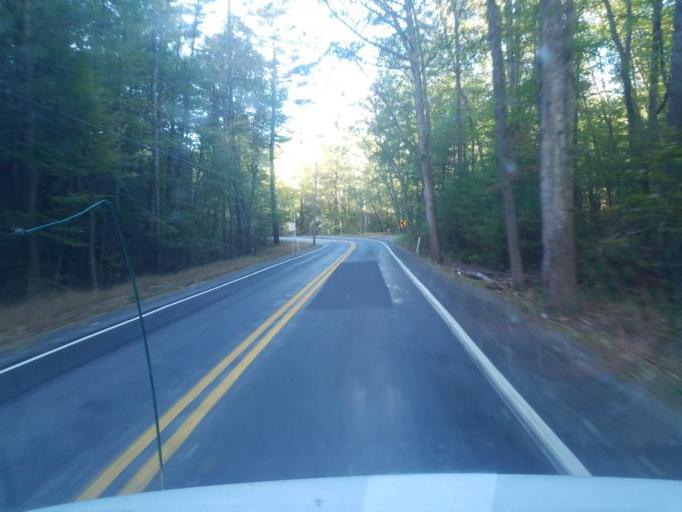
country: US
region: Pennsylvania
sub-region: Franklin County
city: Fayetteville
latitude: 39.8882
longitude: -77.4876
